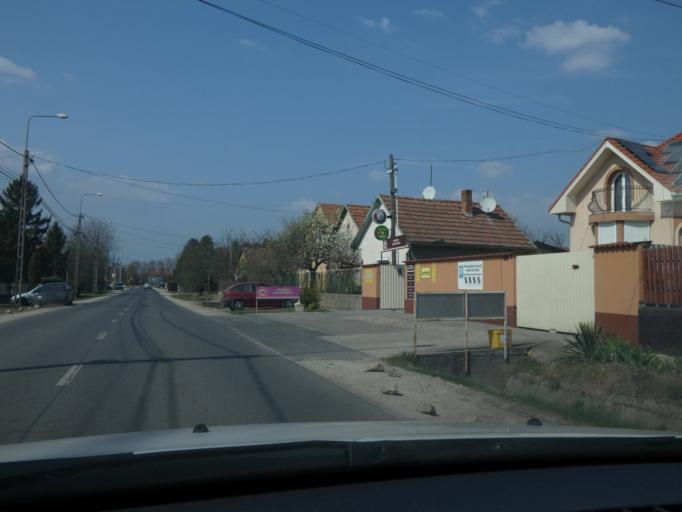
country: HU
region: Pest
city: Ocsa
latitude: 47.3014
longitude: 19.2196
